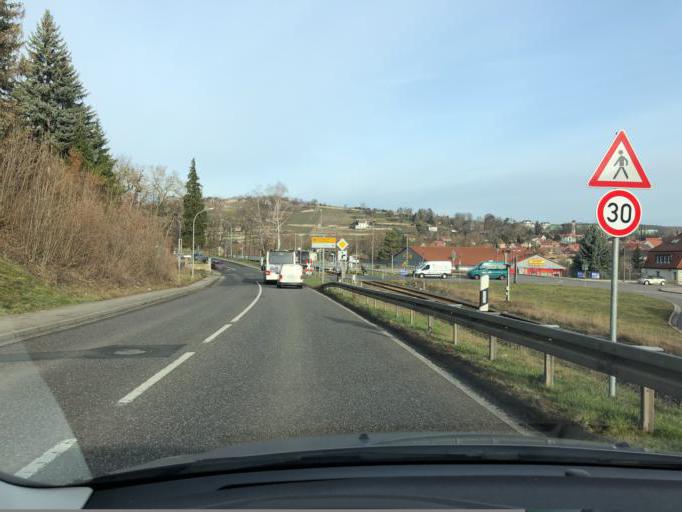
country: DE
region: Saxony-Anhalt
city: Freyburg
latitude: 51.2083
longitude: 11.7682
